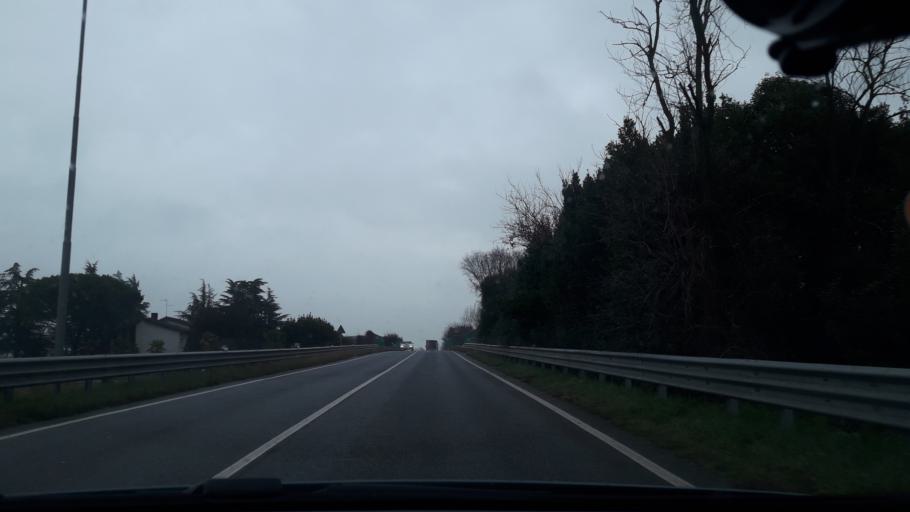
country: IT
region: Friuli Venezia Giulia
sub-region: Provincia di Udine
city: Basaldella
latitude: 46.0206
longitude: 13.2134
